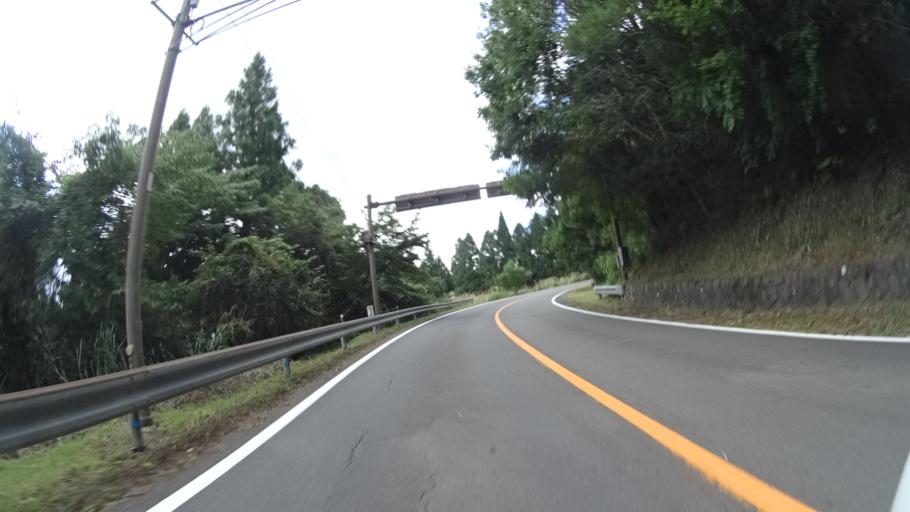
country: JP
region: Oita
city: Tsukawaki
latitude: 33.2478
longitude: 131.2940
